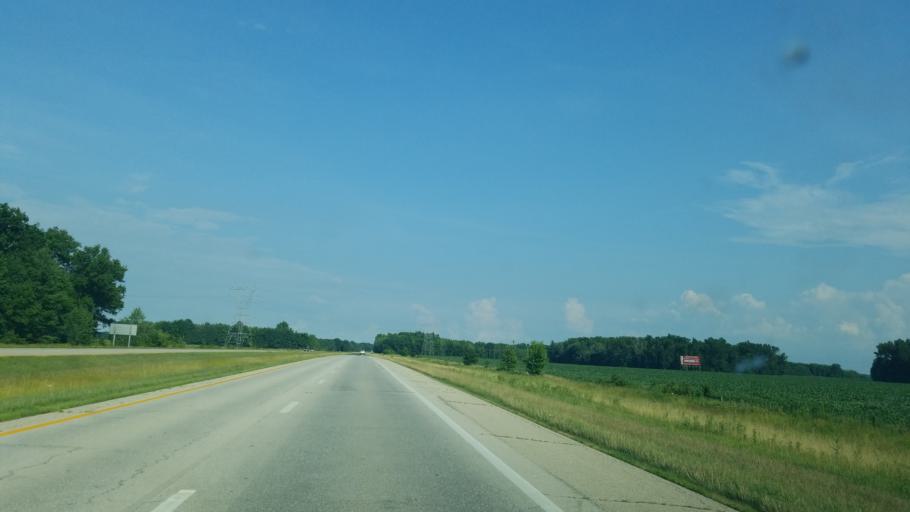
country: US
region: Ohio
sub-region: Brown County
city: Mount Orab
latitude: 39.0331
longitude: -83.8959
